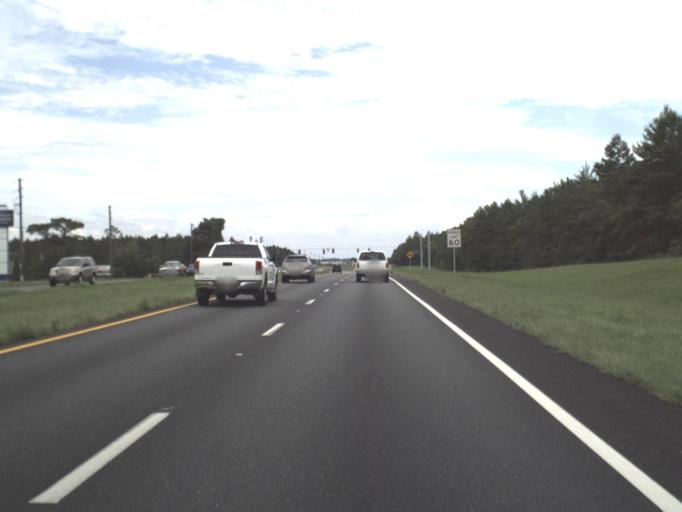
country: US
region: Florida
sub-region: Citrus County
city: Citrus Hills
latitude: 28.8575
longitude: -82.4224
